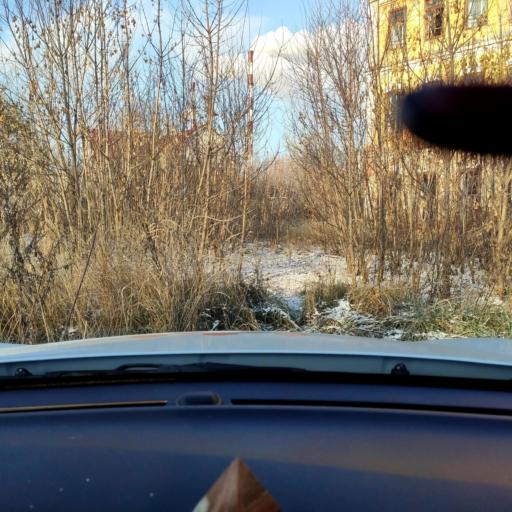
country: RU
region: Tatarstan
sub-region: Gorod Kazan'
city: Kazan
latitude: 55.8179
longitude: 49.0538
